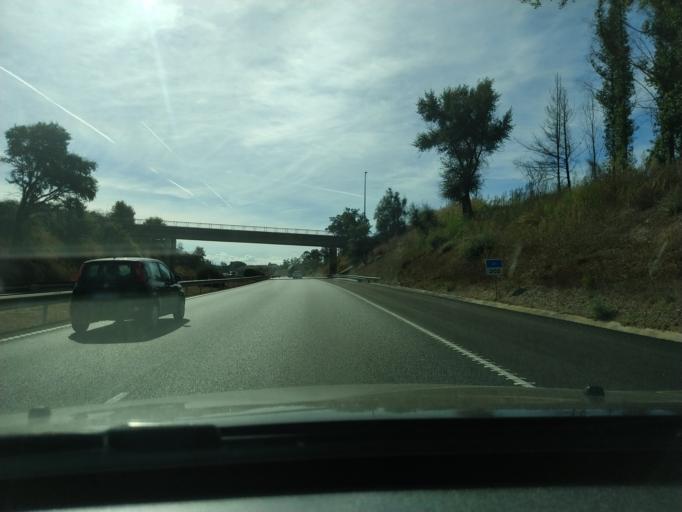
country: PT
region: Aveiro
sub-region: Mealhada
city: Pampilhosa do Botao
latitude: 40.3101
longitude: -8.4892
